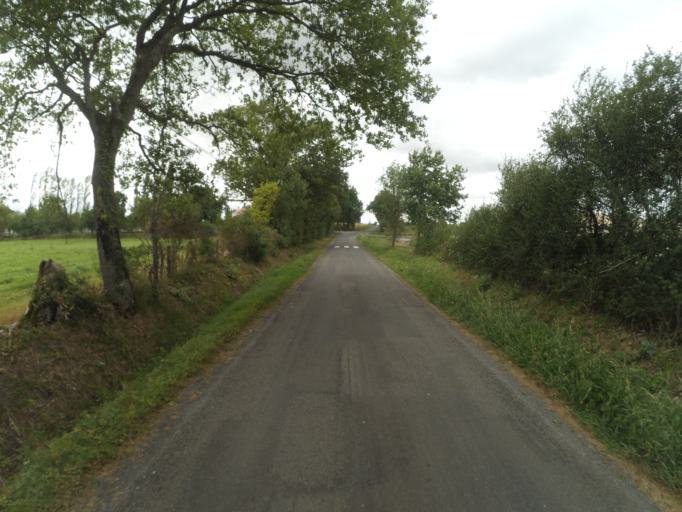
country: FR
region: Pays de la Loire
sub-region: Departement de la Vendee
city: Saint-Philbert-de-Bouaine
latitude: 46.9951
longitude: -1.5245
